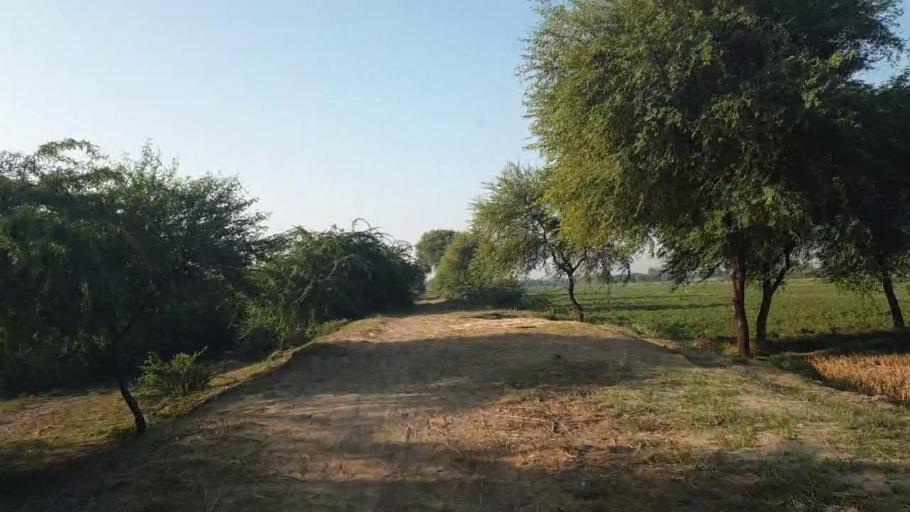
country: PK
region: Sindh
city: Badin
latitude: 24.6099
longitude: 68.7831
